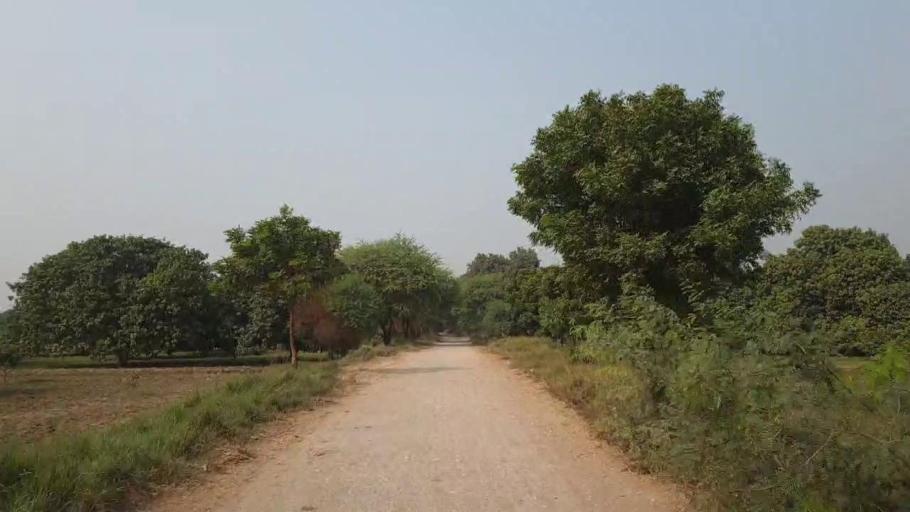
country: PK
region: Sindh
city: Tando Muhammad Khan
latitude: 25.2097
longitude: 68.5592
